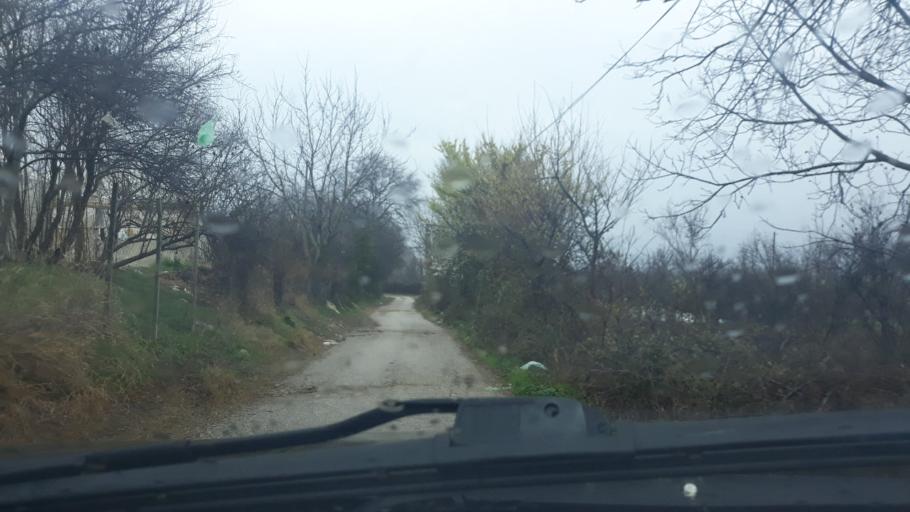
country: MK
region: Valandovo
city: Valandovo
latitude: 41.3173
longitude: 22.5491
